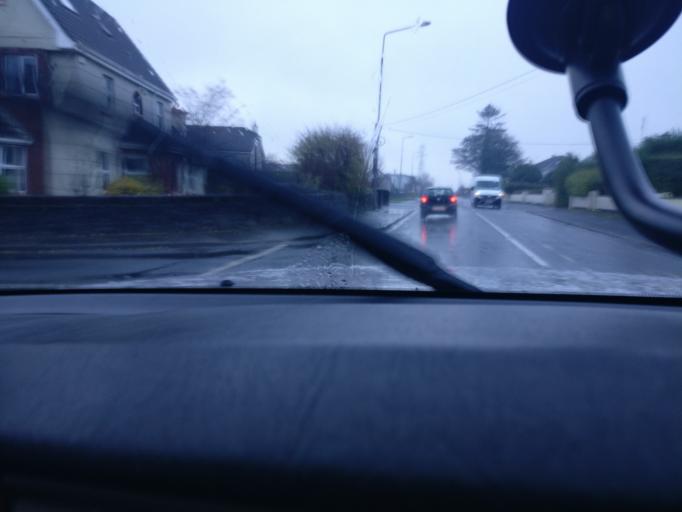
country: IE
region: Connaught
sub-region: County Galway
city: Gaillimh
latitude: 53.2910
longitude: -8.9946
